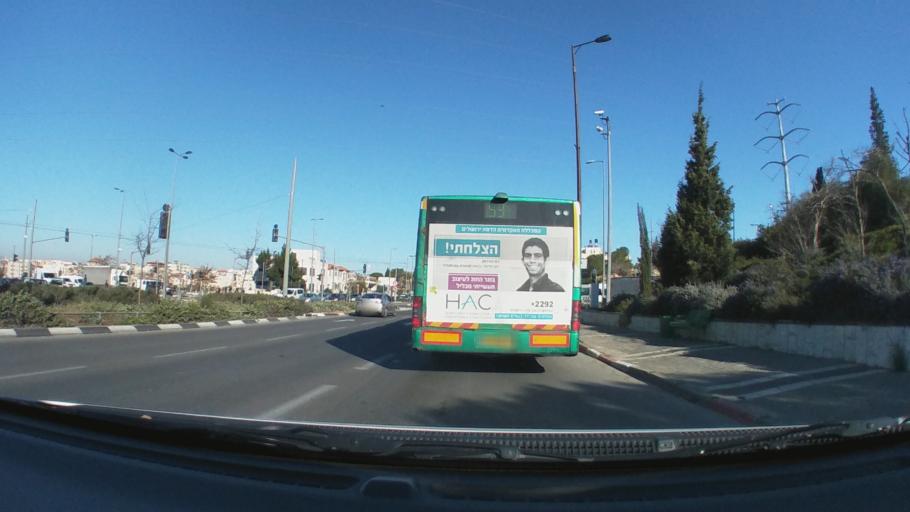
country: PS
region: West Bank
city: East Jerusalem
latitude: 31.8058
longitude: 35.2347
